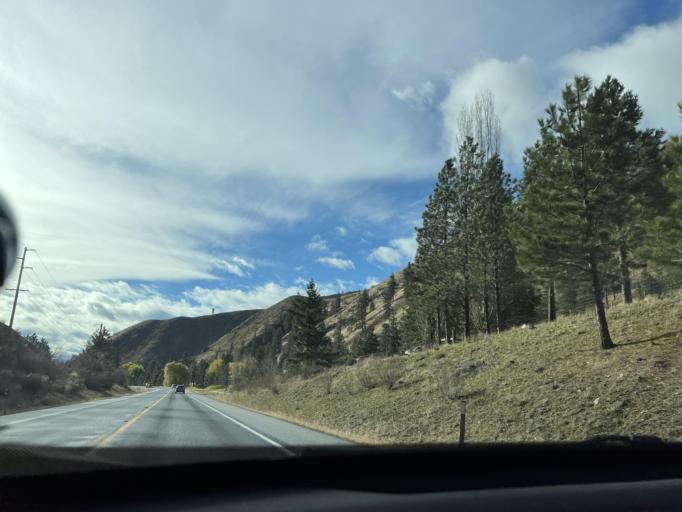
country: US
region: Washington
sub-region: Chelan County
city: Manson
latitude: 47.8136
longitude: -120.1319
